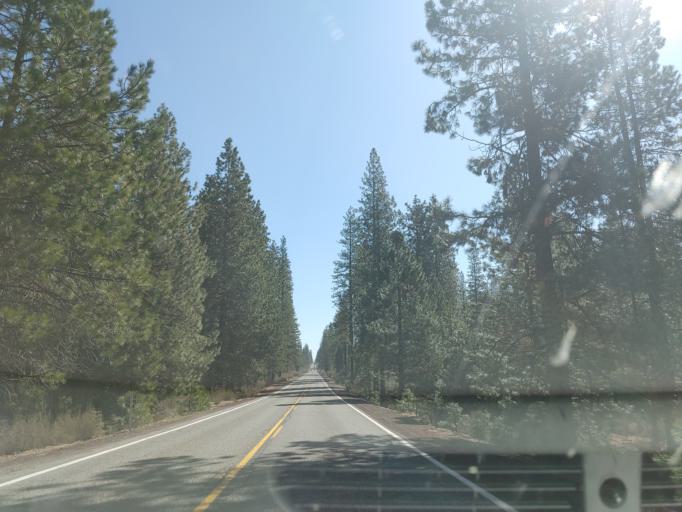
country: US
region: California
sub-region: Siskiyou County
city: McCloud
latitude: 41.2553
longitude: -122.0559
